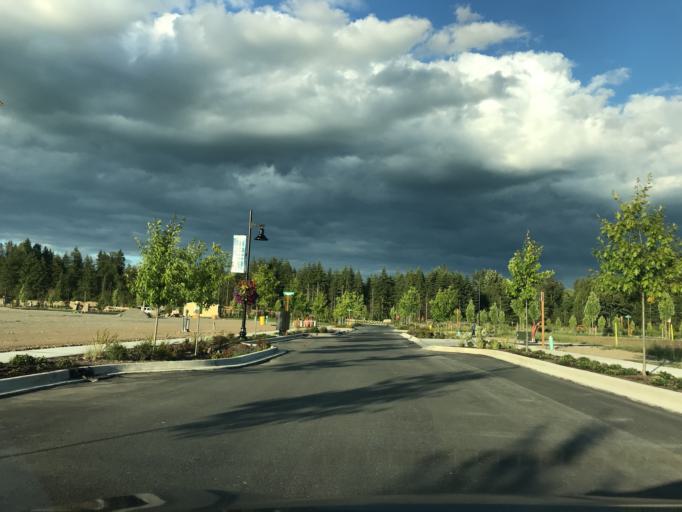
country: US
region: Washington
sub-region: King County
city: Black Diamond
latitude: 47.3093
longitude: -122.0319
